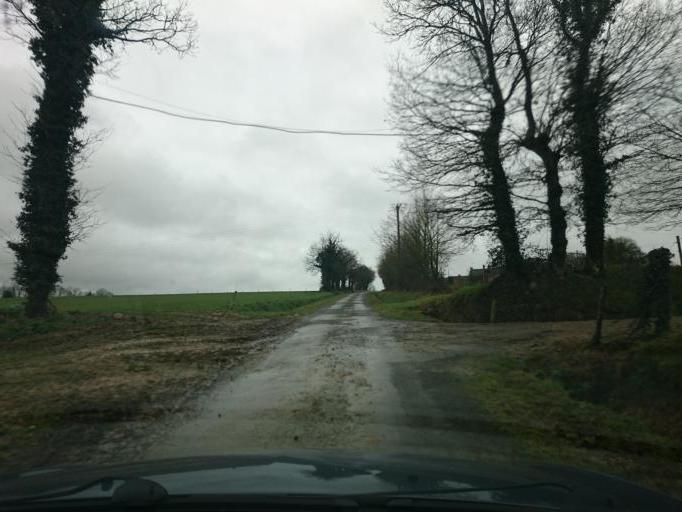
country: FR
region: Brittany
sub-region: Departement d'Ille-et-Vilaine
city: Chanteloup
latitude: 47.9392
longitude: -1.5969
